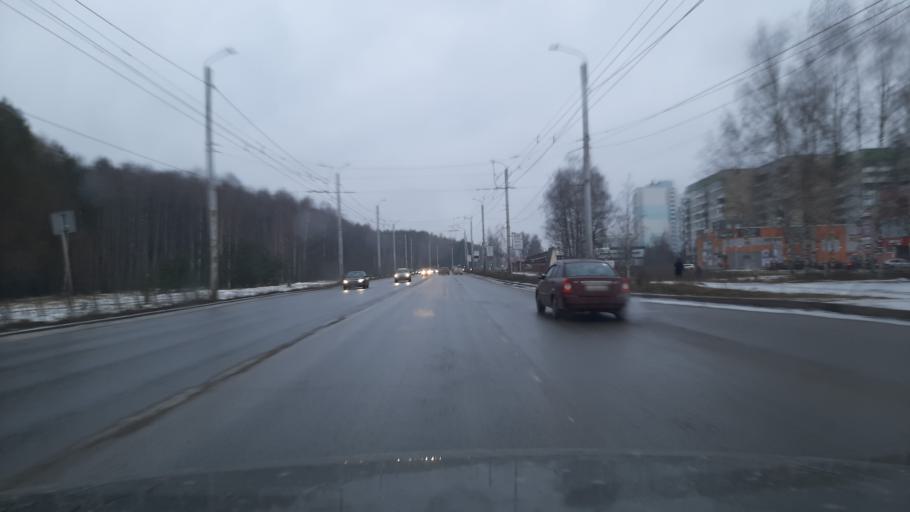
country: RU
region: Ivanovo
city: Kokhma
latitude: 56.9494
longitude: 41.0500
